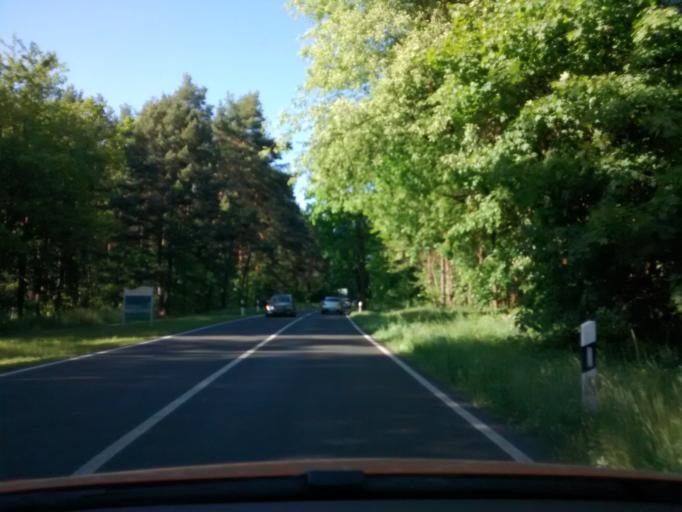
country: DE
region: Brandenburg
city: Bad Saarow
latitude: 52.3067
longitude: 14.0622
